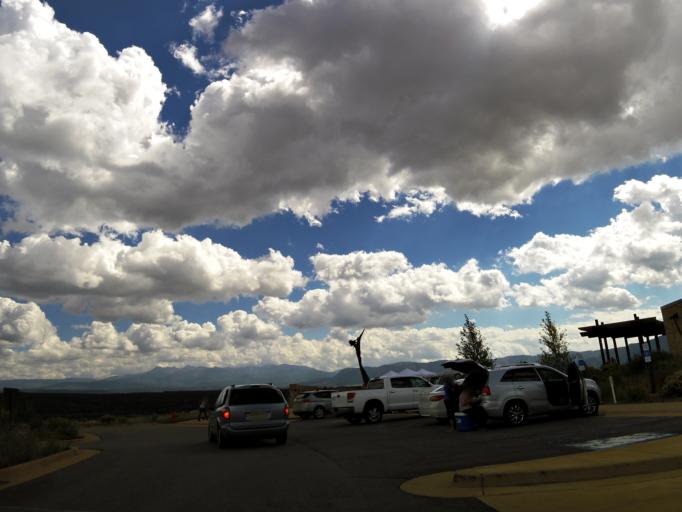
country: US
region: Colorado
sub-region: Montezuma County
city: Mancos
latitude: 37.3362
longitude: -108.4082
